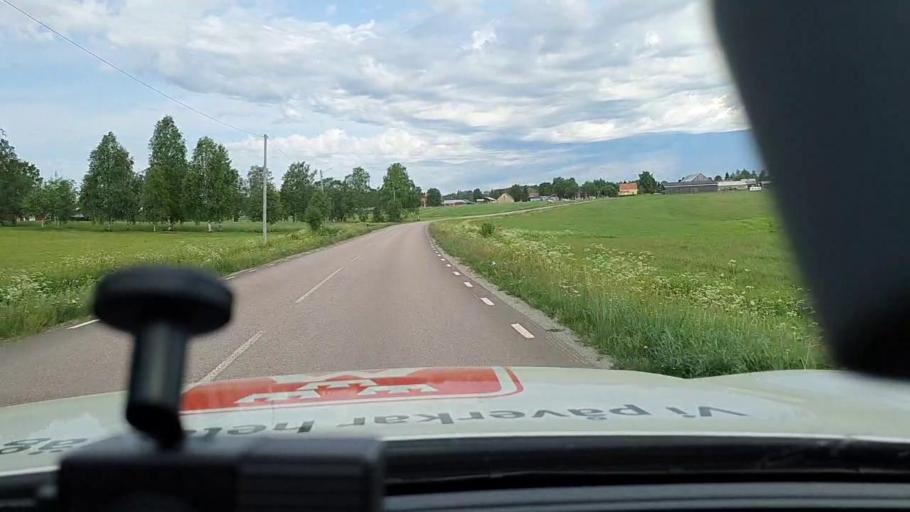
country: SE
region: Norrbotten
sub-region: Bodens Kommun
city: Saevast
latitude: 65.7054
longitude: 21.7651
